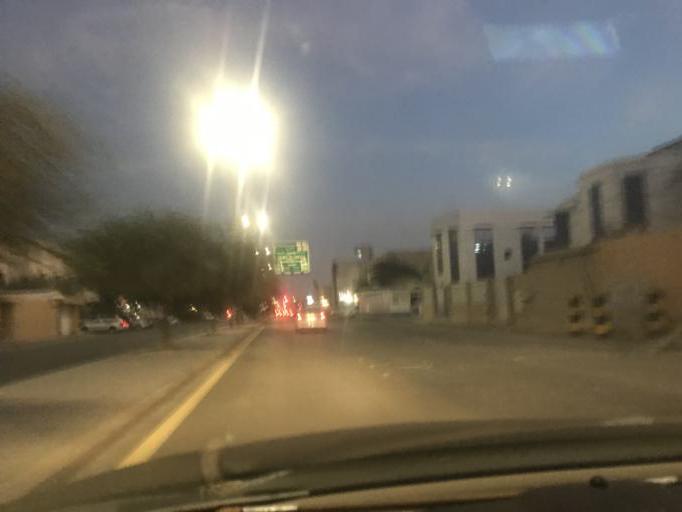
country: SA
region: Ar Riyad
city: Riyadh
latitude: 24.7331
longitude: 46.7605
